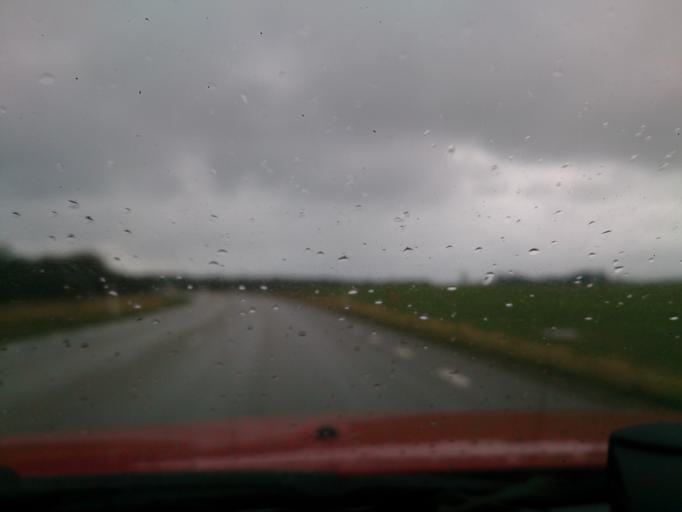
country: SE
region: Skane
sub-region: Ystads Kommun
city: Ystad
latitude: 55.4335
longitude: 13.7768
